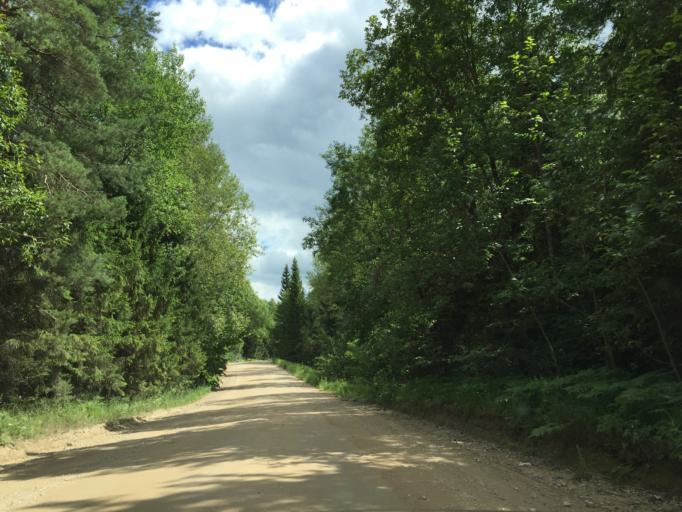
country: LV
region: Ropazu
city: Ropazi
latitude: 56.9130
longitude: 24.7547
